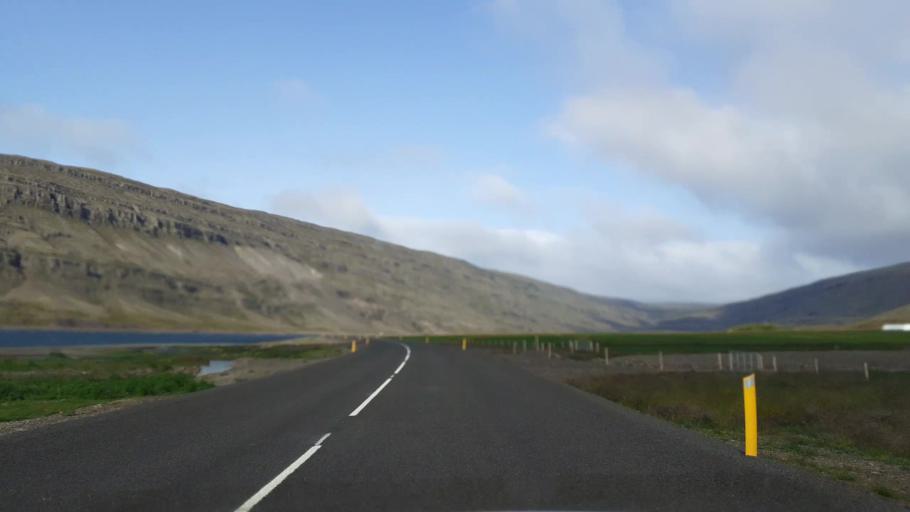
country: IS
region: East
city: Reydarfjoerdur
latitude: 64.7890
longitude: -14.4541
